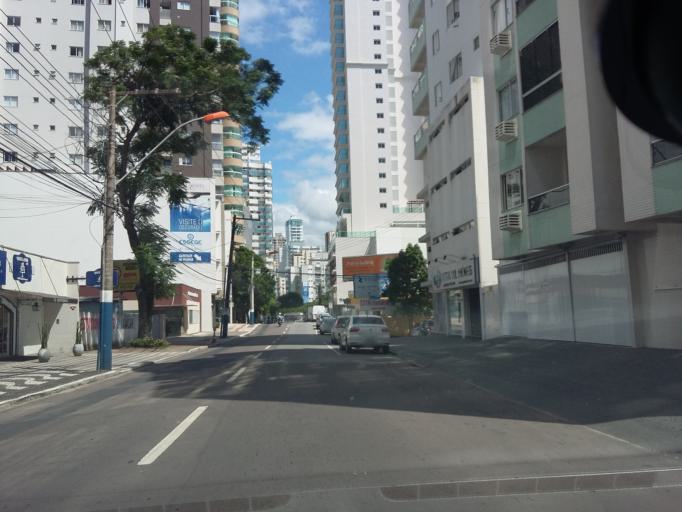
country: BR
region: Santa Catarina
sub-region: Balneario Camboriu
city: Balneario Camboriu
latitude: -26.9735
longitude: -48.6362
